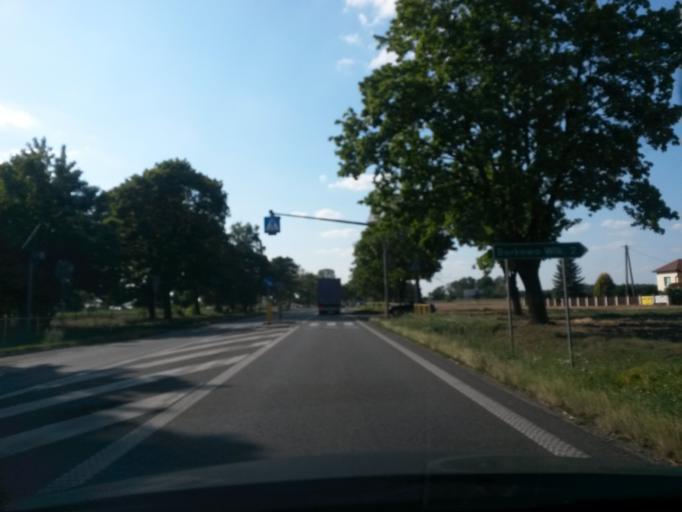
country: PL
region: Masovian Voivodeship
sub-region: Powiat sierpecki
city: Sierpc
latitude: 52.8447
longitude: 19.7169
